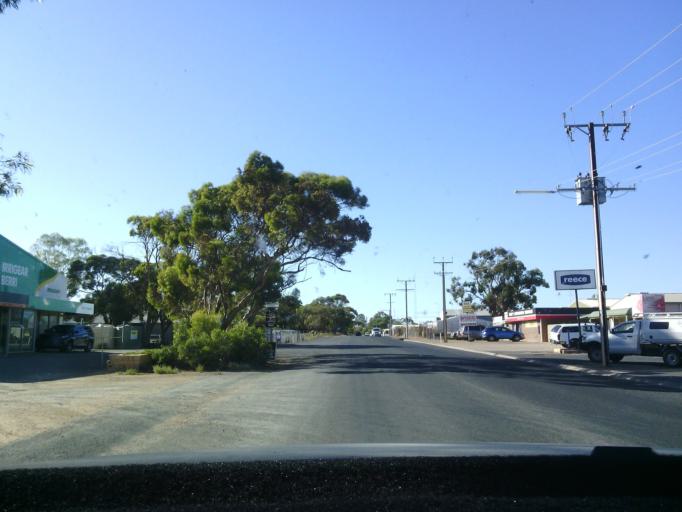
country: AU
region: South Australia
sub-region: Berri and Barmera
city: Berri
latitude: -34.2685
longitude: 140.6034
